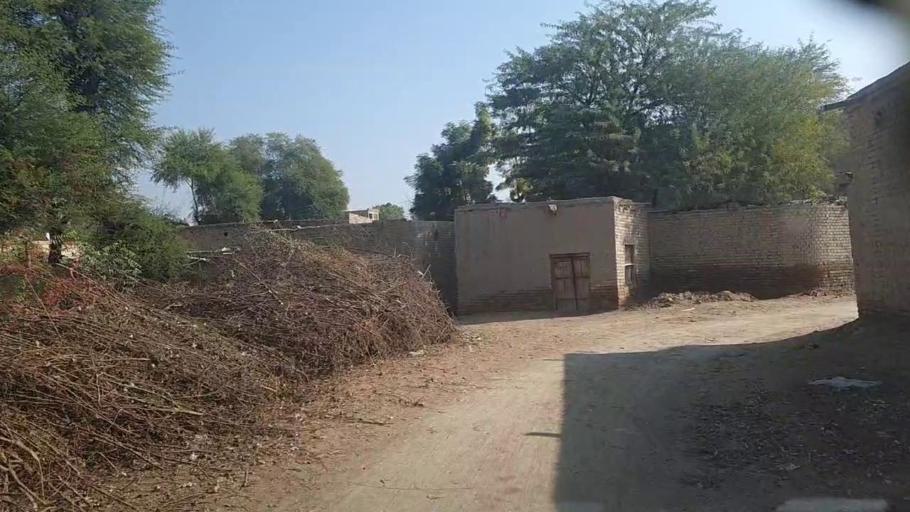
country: PK
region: Sindh
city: Kandiari
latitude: 27.0248
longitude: 68.5063
